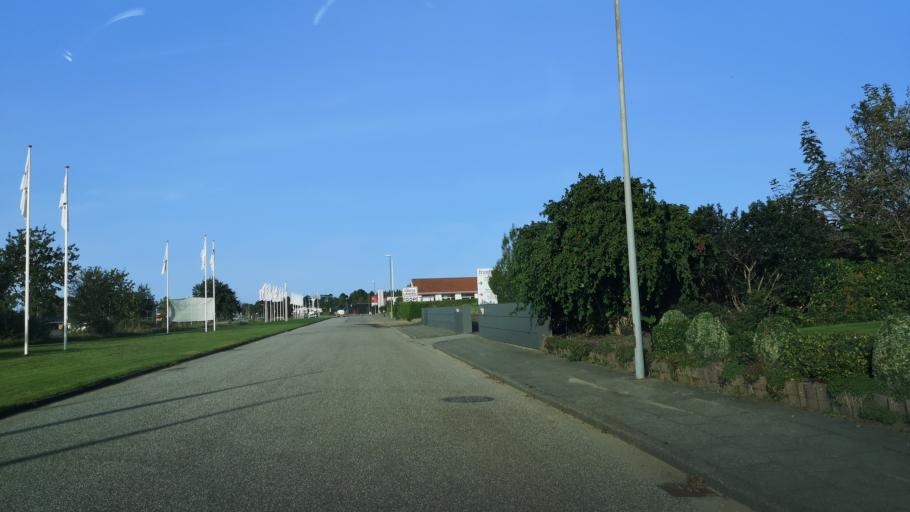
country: DK
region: Central Jutland
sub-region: Herning Kommune
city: Snejbjerg
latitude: 56.1348
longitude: 8.9172
